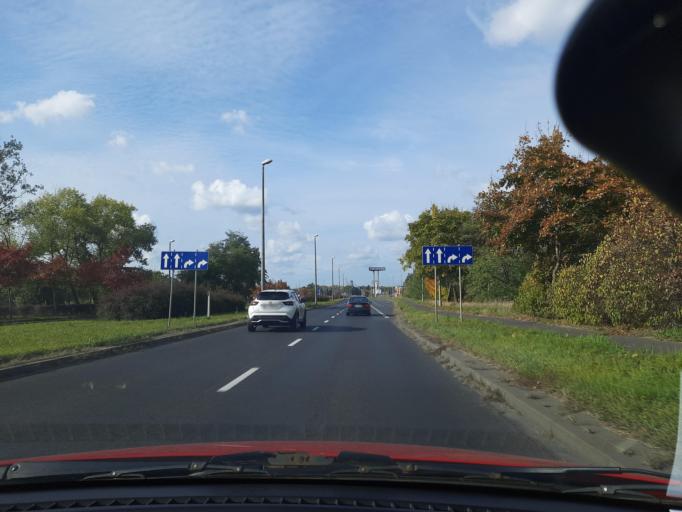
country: PL
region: Kujawsko-Pomorskie
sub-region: Powiat torunski
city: Wielka Nieszawka
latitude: 53.0163
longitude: 18.5401
